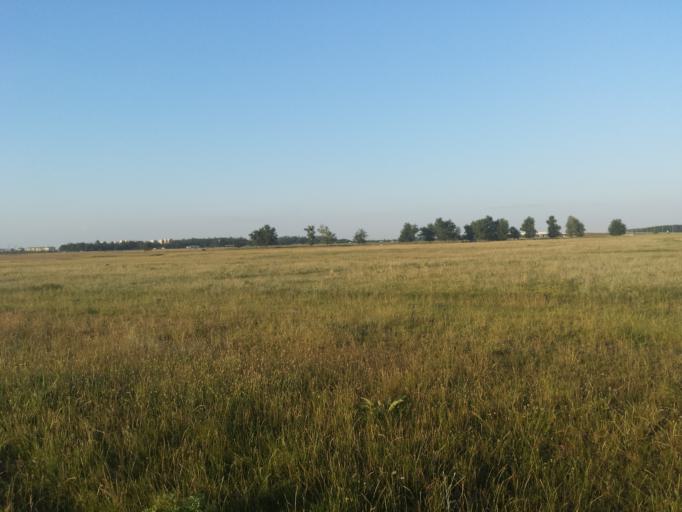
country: RO
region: Ilfov
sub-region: Comuna Tunari
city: Tunari
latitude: 44.5174
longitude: 26.1528
